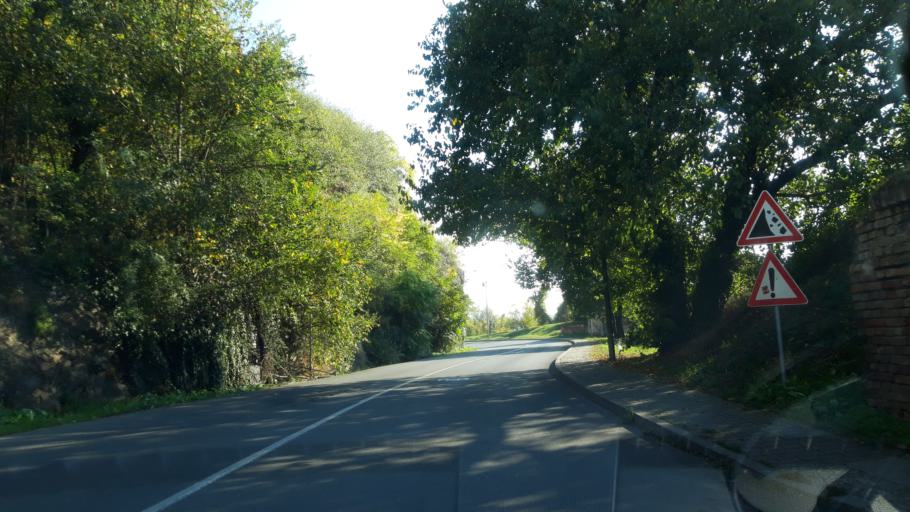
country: RS
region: Autonomna Pokrajina Vojvodina
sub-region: Juznobacki Okrug
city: Petrovaradin
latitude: 45.2529
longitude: 19.8604
